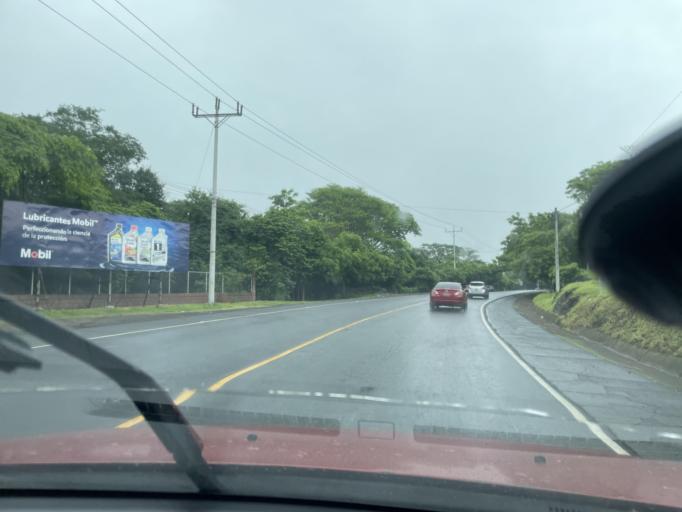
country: SV
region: San Miguel
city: San Miguel
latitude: 13.5590
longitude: -88.1096
